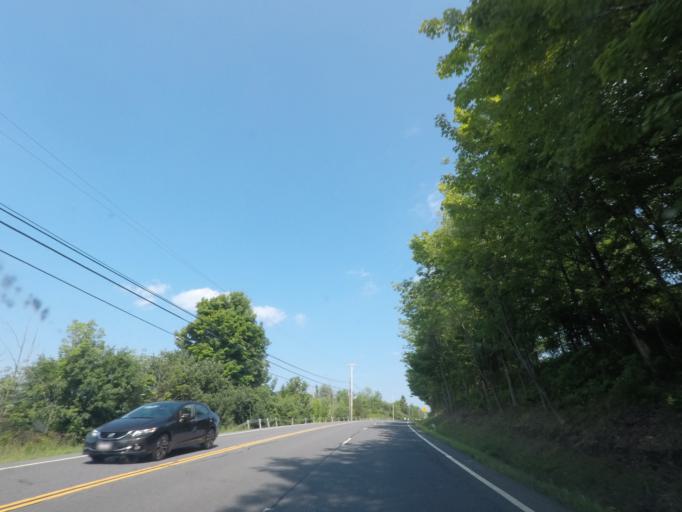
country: US
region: New York
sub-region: Rensselaer County
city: Nassau
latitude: 42.5179
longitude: -73.5827
